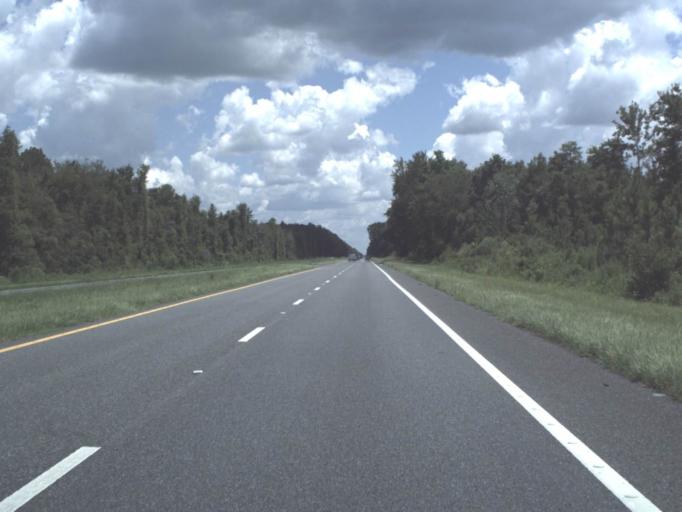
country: US
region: Florida
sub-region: Taylor County
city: Perry
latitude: 30.2652
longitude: -83.7138
